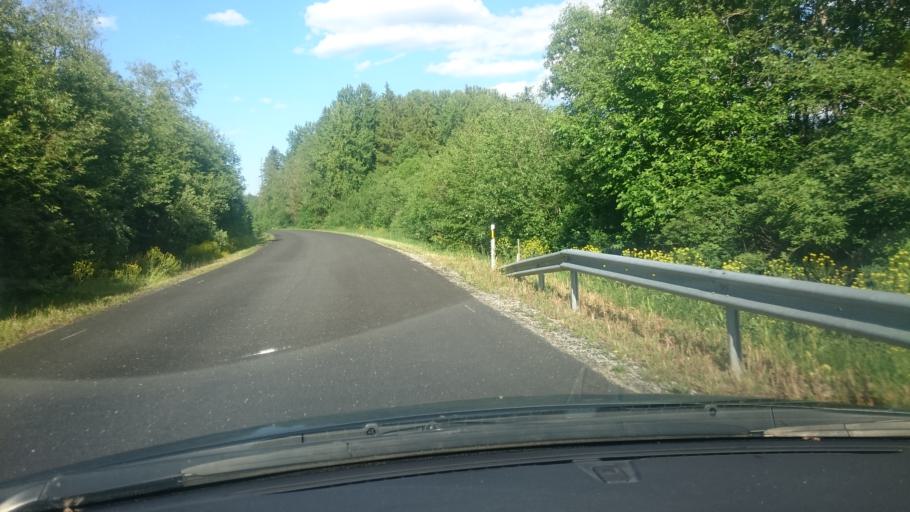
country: EE
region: Harju
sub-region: Rae vald
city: Vaida
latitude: 59.2276
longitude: 25.0071
